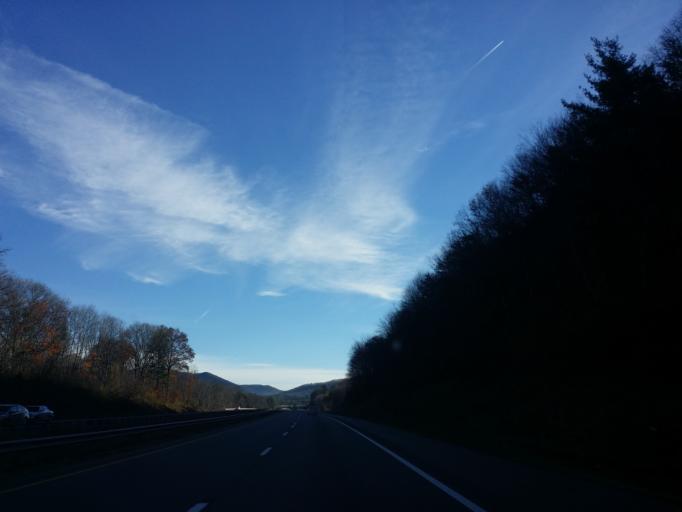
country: US
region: North Carolina
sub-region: Buncombe County
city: Black Mountain
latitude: 35.6026
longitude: -82.3529
